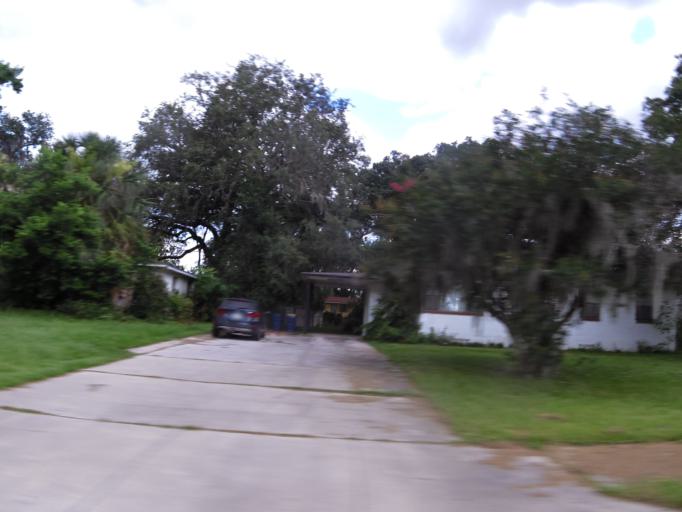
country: US
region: Florida
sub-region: Duval County
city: Jacksonville
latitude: 30.4239
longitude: -81.6827
